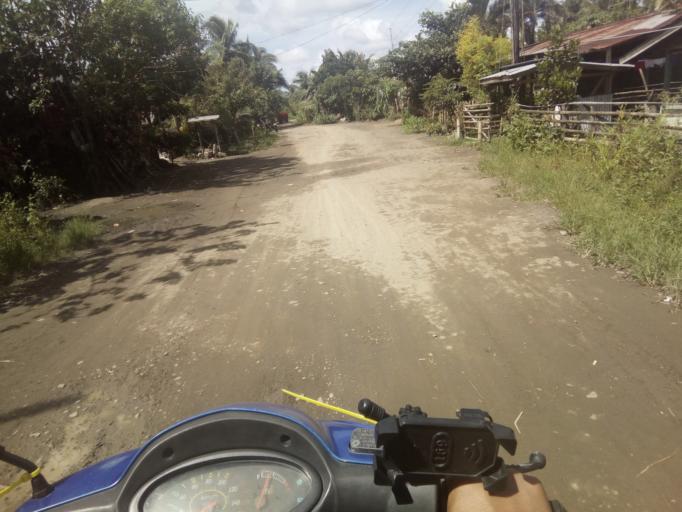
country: PH
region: Caraga
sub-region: Province of Agusan del Sur
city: Santa Josefa
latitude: 7.9630
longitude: 126.0111
